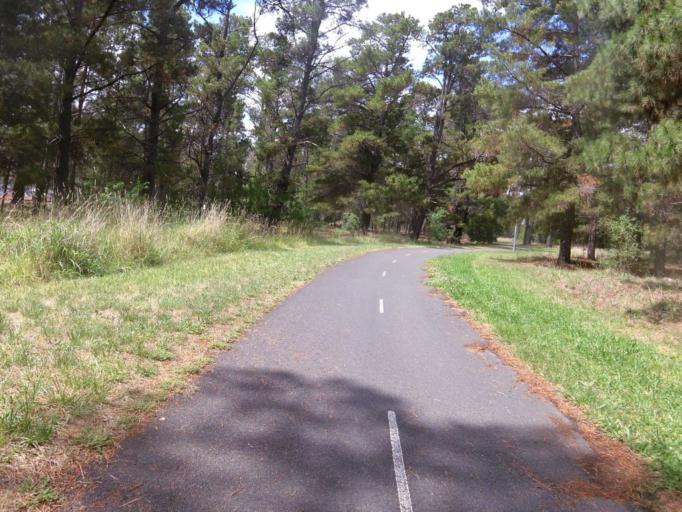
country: AU
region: Australian Capital Territory
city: Macarthur
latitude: -35.4147
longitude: 149.1151
